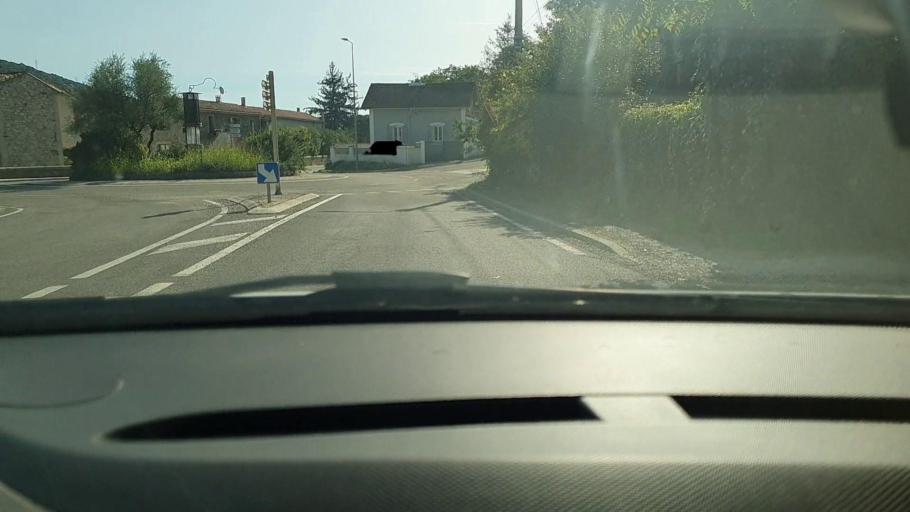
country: FR
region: Languedoc-Roussillon
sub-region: Departement du Gard
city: Saint-Florent-sur-Auzonnet
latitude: 44.2482
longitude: 4.0906
